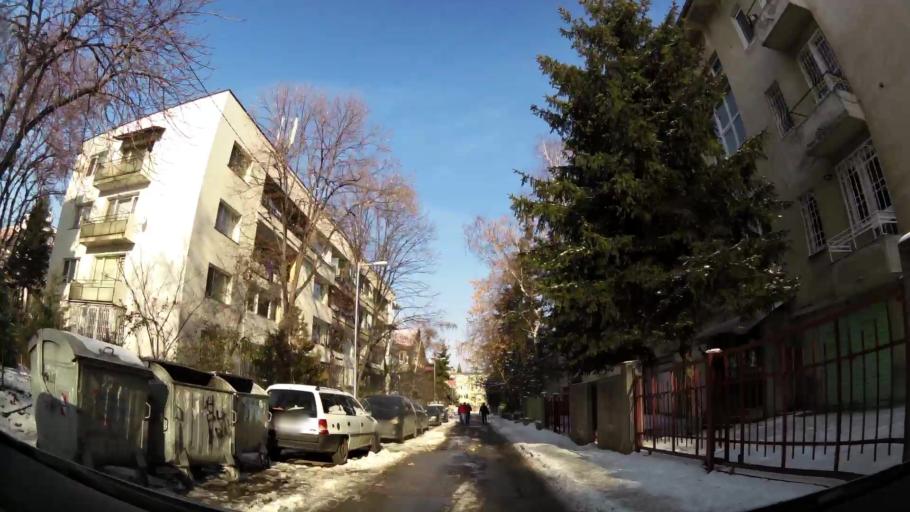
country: BG
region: Sofia-Capital
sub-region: Stolichna Obshtina
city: Sofia
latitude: 42.6739
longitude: 23.3531
